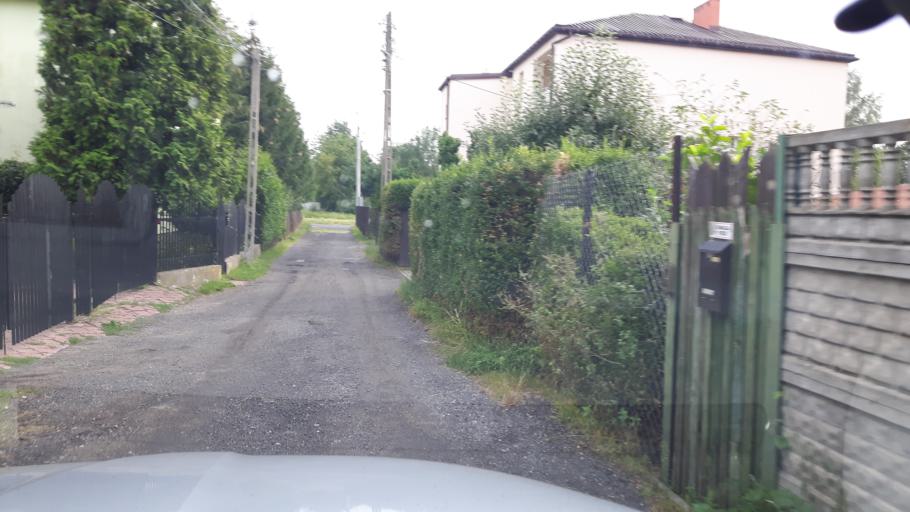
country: PL
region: Masovian Voivodeship
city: Zielonka
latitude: 52.3136
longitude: 21.1355
